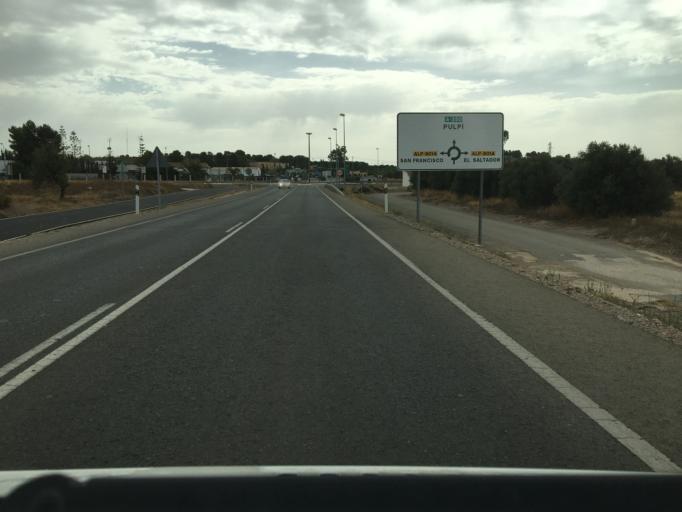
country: ES
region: Andalusia
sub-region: Provincia de Almeria
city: Huercal-Overa
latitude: 37.4171
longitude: -1.8801
